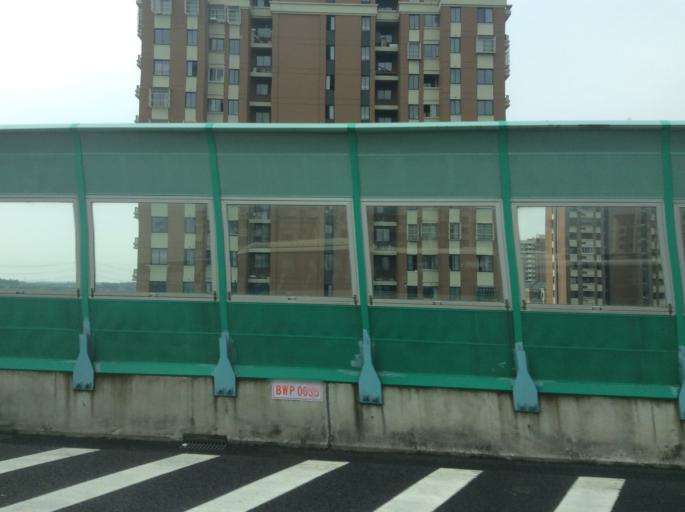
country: CN
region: Shanghai Shi
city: Kangqiao
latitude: 31.1899
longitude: 121.6343
